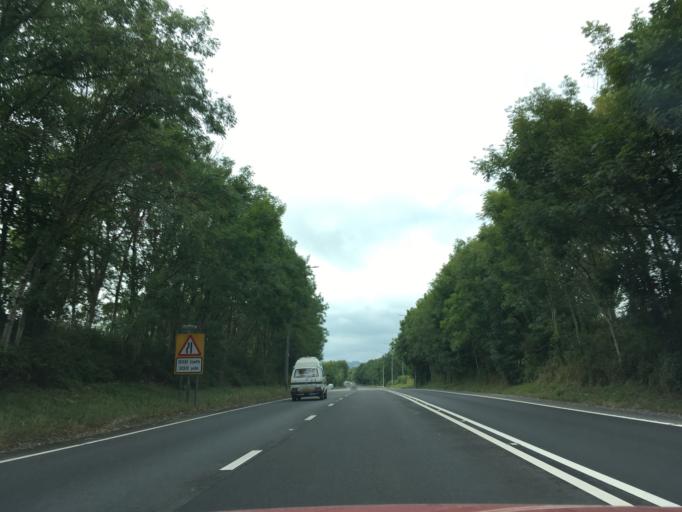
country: GB
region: Wales
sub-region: Carmarthenshire
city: Saint Clears
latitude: 51.8195
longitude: -4.5139
